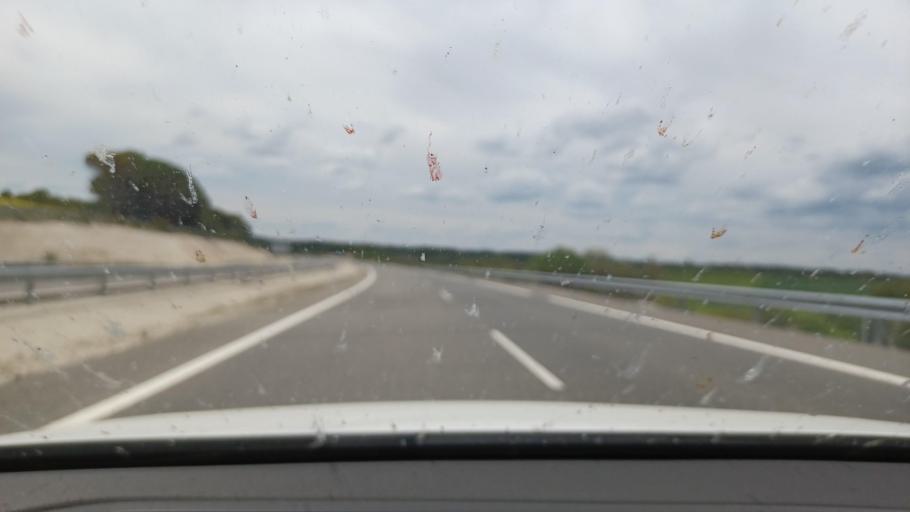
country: ES
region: Castille and Leon
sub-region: Provincia de Valladolid
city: Viloria
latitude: 41.4413
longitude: -4.3959
